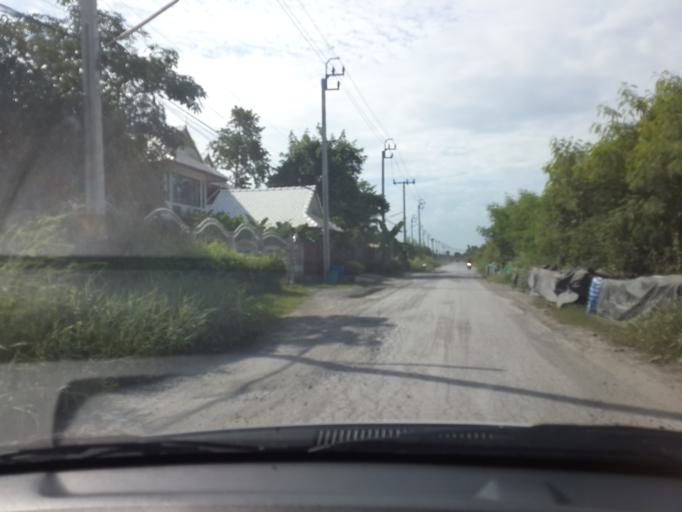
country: TH
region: Bangkok
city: Nong Chok
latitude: 13.8538
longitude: 100.8002
